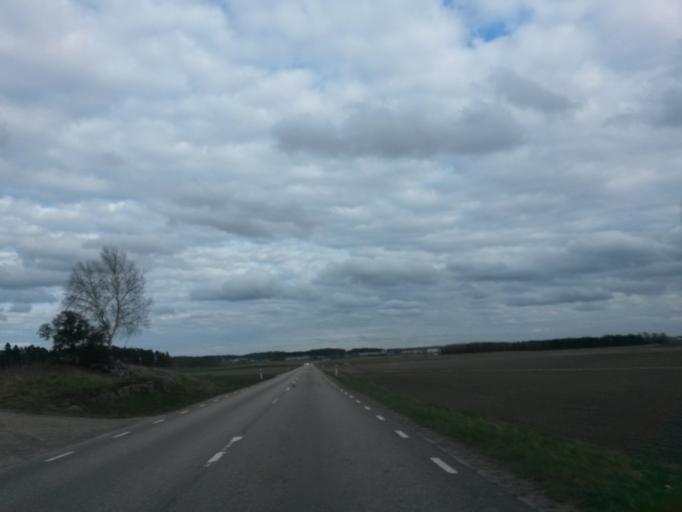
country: SE
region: Vaestra Goetaland
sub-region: Vargarda Kommun
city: Vargarda
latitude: 58.0500
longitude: 12.7766
